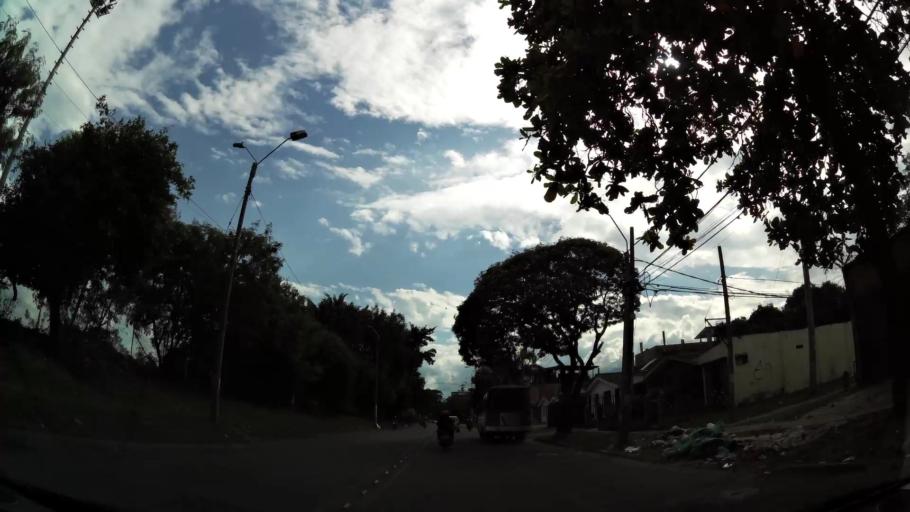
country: CO
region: Valle del Cauca
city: Cali
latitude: 3.4741
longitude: -76.5151
